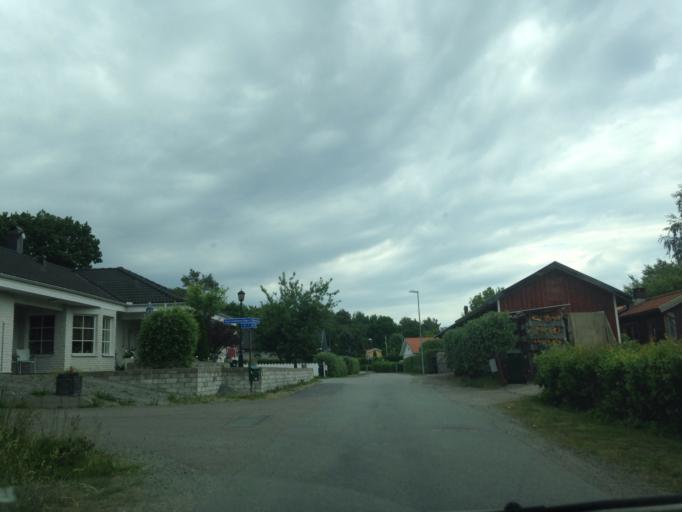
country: SE
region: Vaestra Goetaland
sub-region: Goteborg
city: Torslanda
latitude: 57.7688
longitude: 11.8392
